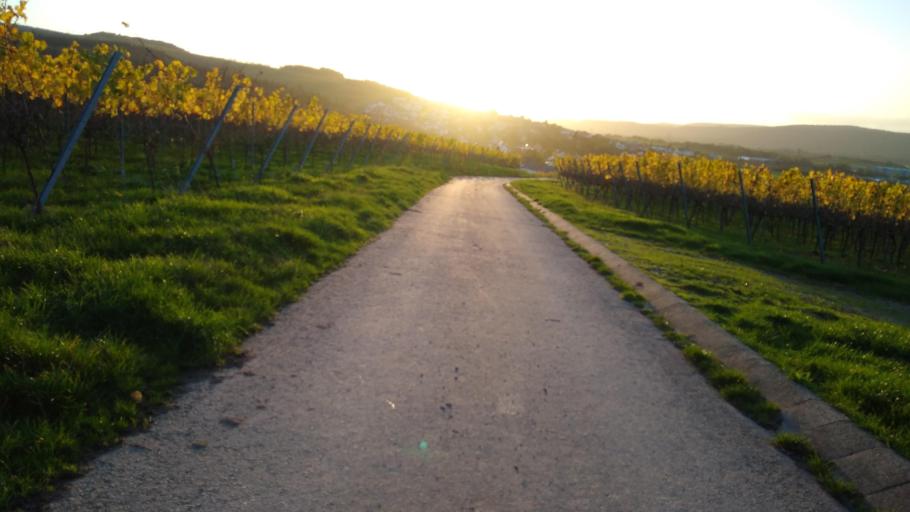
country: DE
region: Rheinland-Pfalz
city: Bekond
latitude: 49.8528
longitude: 6.8171
